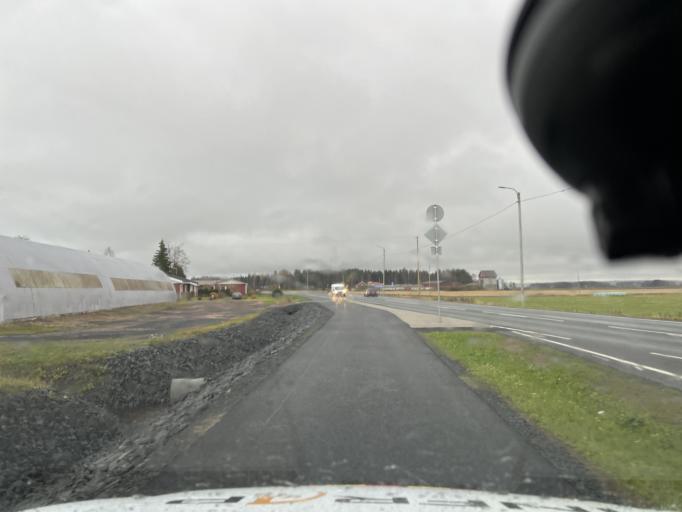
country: FI
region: Northern Ostrobothnia
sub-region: Ylivieska
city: Sievi
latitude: 63.9511
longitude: 24.5150
